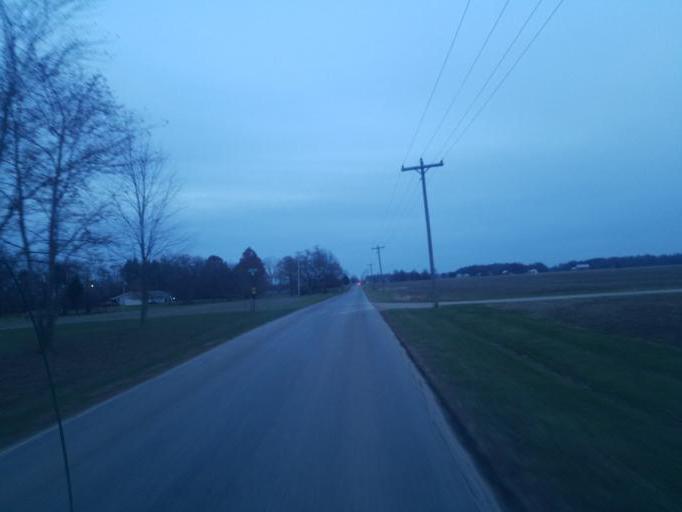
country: US
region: Indiana
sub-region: Adams County
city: Berne
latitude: 40.7301
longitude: -84.9852
